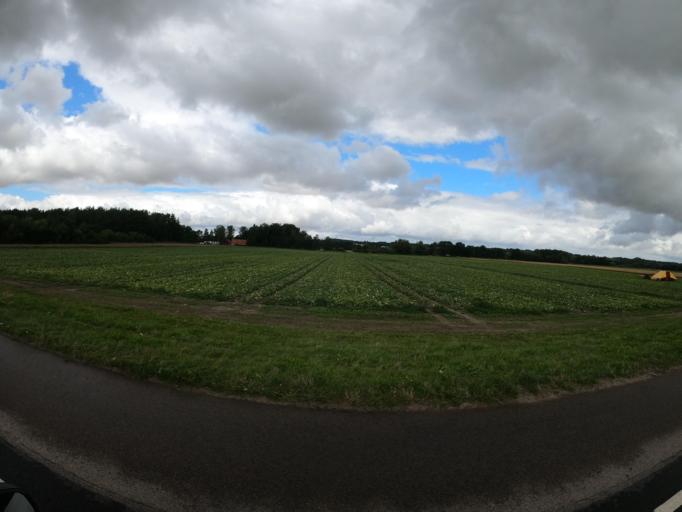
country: SE
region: Skane
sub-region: Hoors Kommun
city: Loberod
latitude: 55.7297
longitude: 13.4201
